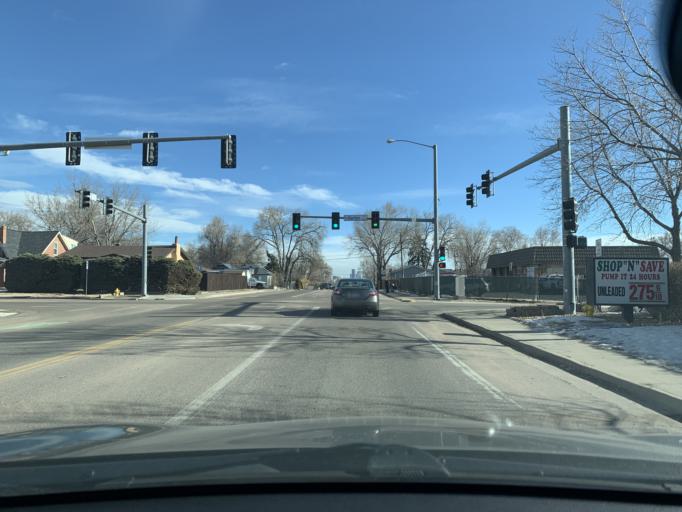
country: US
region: Colorado
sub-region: Jefferson County
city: Edgewater
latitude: 39.7476
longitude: -105.0630
